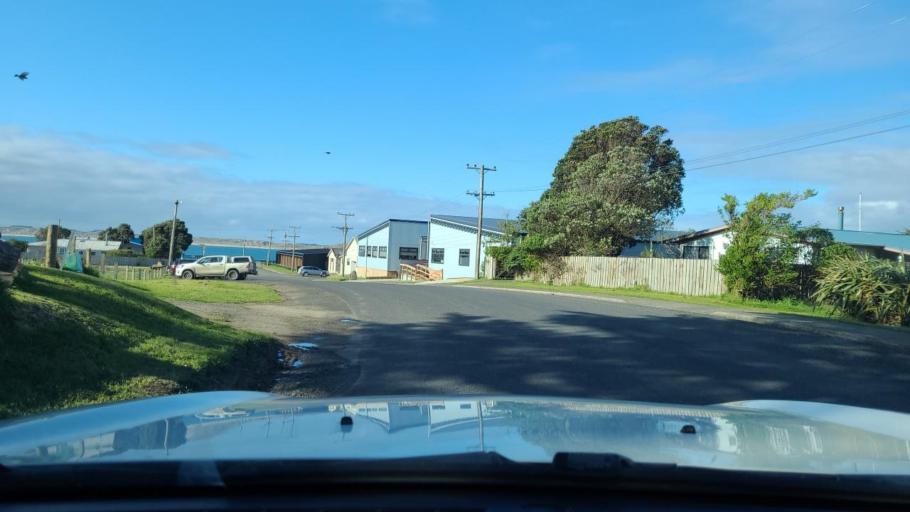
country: NZ
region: Chatham Islands
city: Waitangi
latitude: -43.9538
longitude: -176.5640
